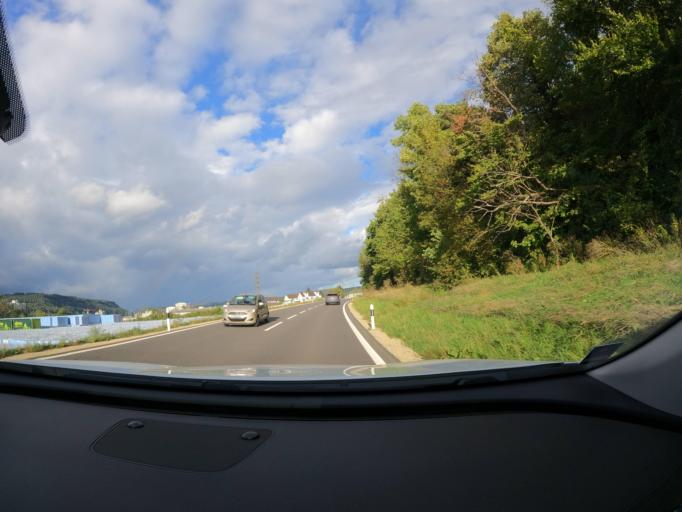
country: CH
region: Aargau
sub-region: Bezirk Brugg
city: Brugg
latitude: 47.4730
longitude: 8.2026
